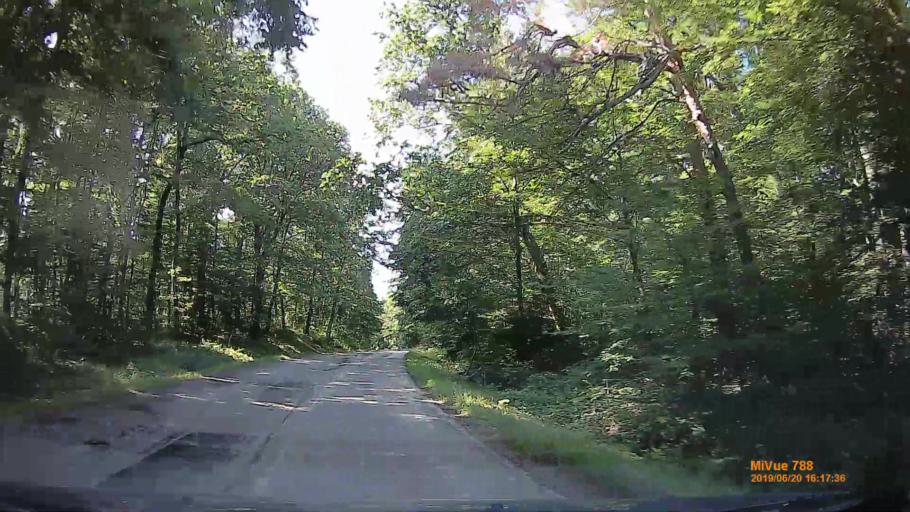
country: HU
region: Baranya
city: Buekkoesd
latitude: 46.1050
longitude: 18.0594
